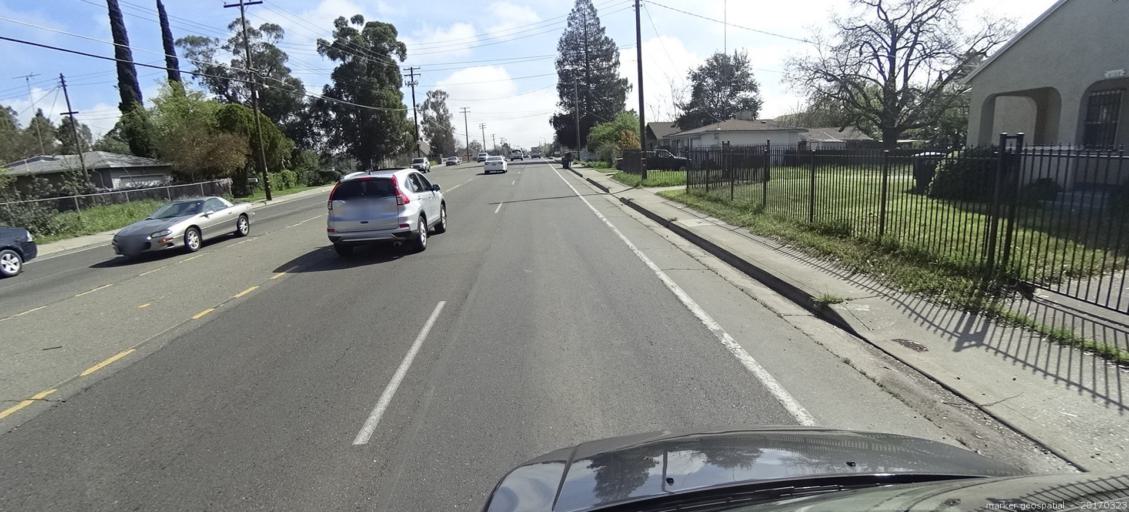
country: US
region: California
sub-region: Sacramento County
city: Florin
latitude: 38.5104
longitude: -121.4327
